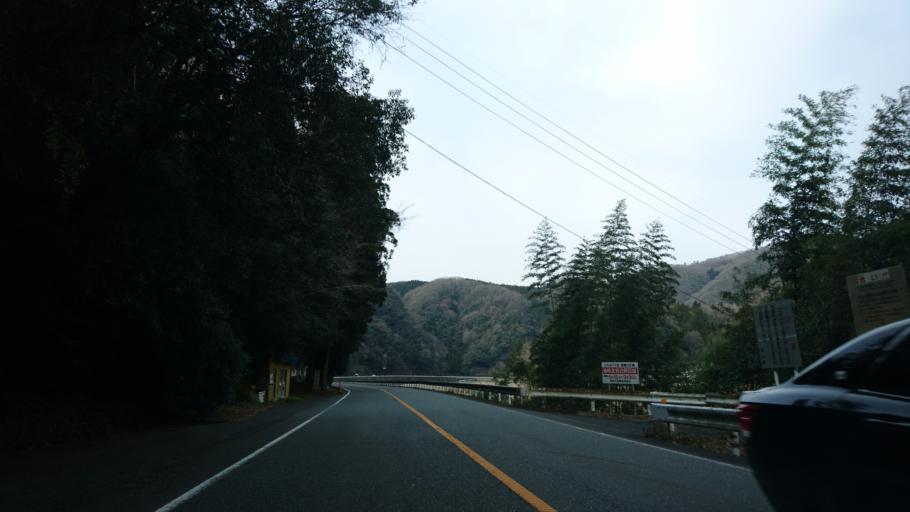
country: JP
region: Okayama
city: Takahashi
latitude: 34.8601
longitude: 133.5690
